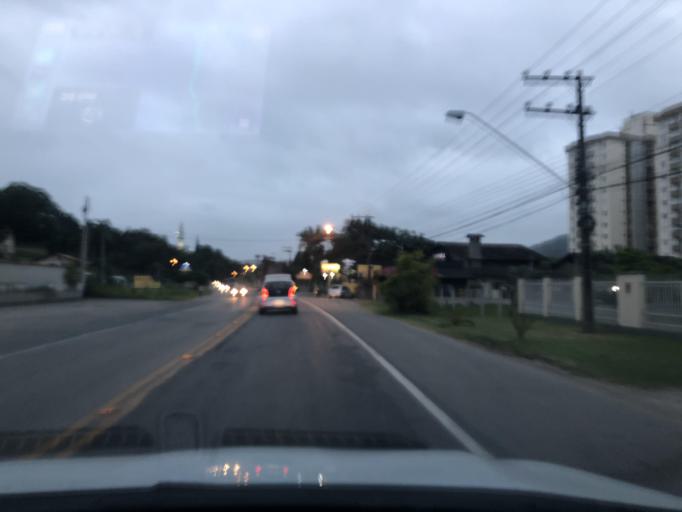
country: BR
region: Santa Catarina
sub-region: Pomerode
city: Pomerode
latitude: -26.7899
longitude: -49.0864
